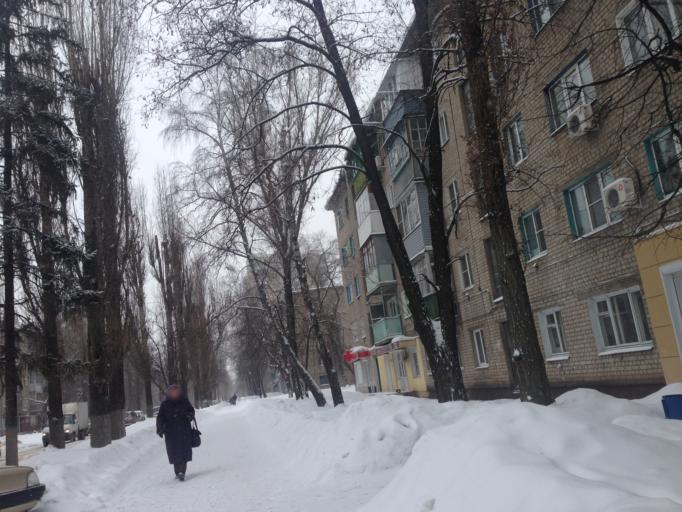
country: RU
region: Voronezj
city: Voronezh
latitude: 51.6546
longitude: 39.1493
